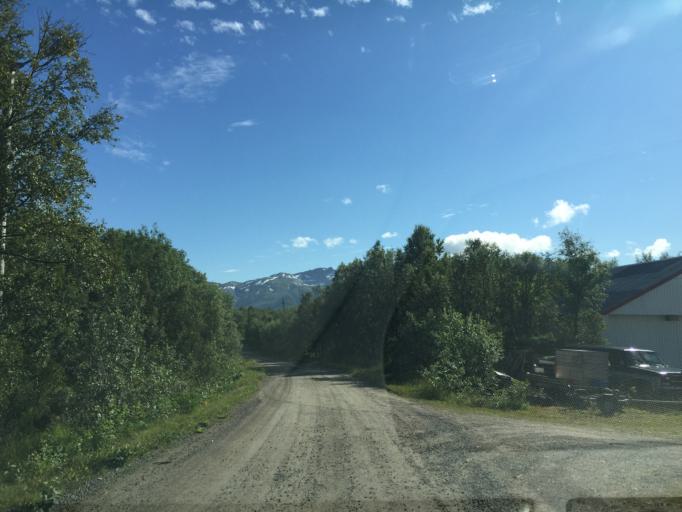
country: NO
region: Nordland
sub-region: Vagan
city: Kabelvag
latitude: 68.3548
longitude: 14.4486
